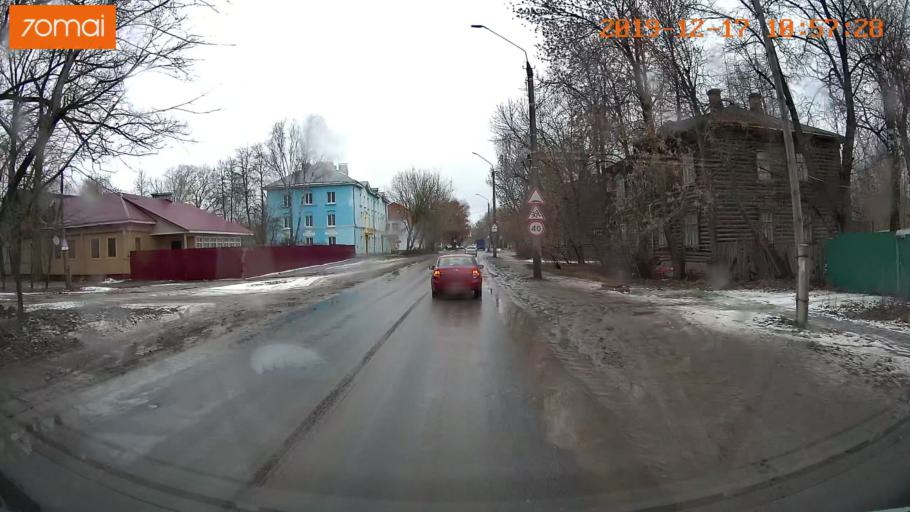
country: RU
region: Vladimir
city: Gus'-Khrustal'nyy
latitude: 55.6211
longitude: 40.6580
